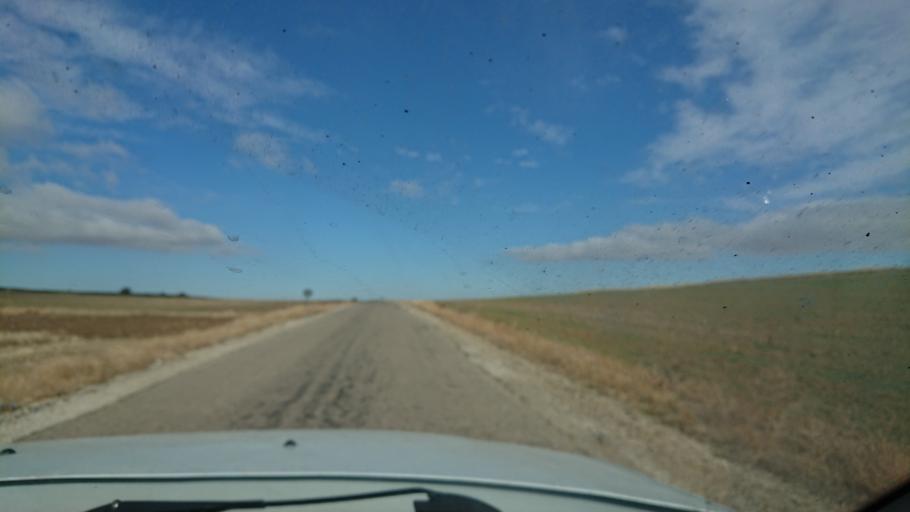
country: TR
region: Aksaray
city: Agacoren
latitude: 38.8376
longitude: 33.9539
